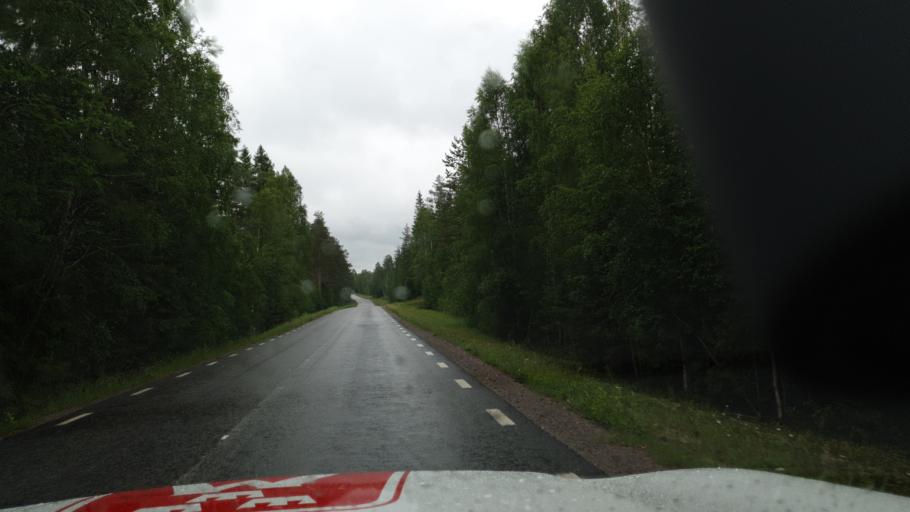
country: SE
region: Vaesterbotten
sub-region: Vannas Kommun
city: Vannasby
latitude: 63.8120
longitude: 19.8560
